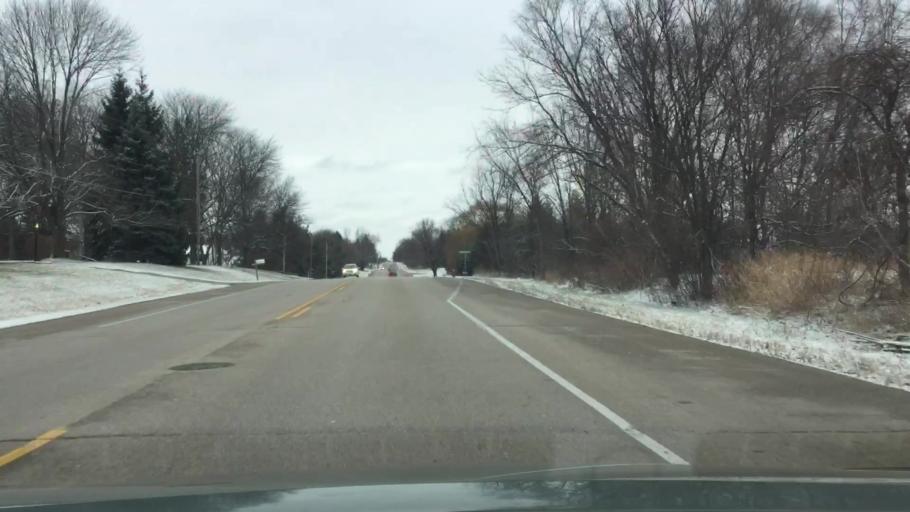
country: US
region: Wisconsin
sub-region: Waukesha County
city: Brookfield
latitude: 43.0925
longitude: -88.1058
